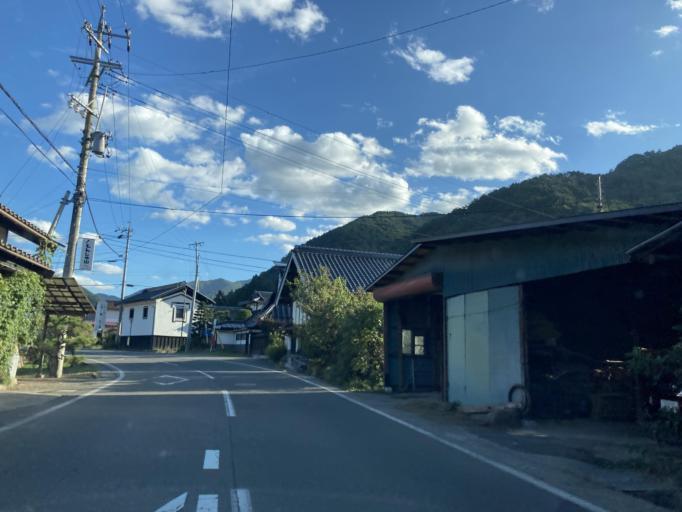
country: JP
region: Nagano
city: Omachi
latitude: 36.4496
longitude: 138.0658
